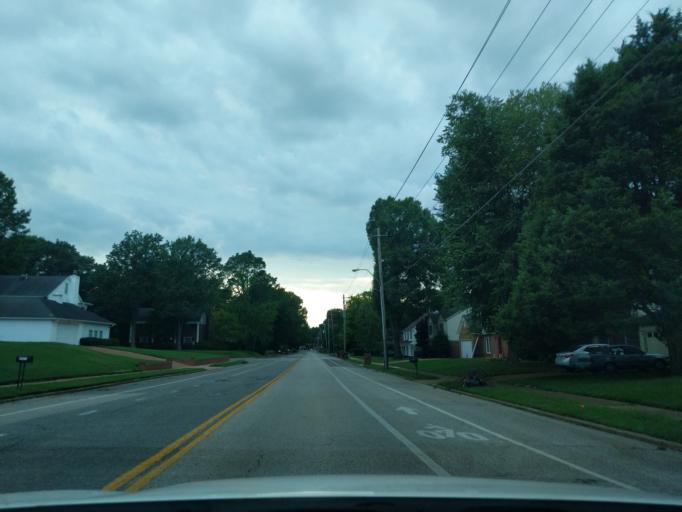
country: US
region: Tennessee
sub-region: Shelby County
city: Germantown
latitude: 35.0768
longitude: -89.8362
